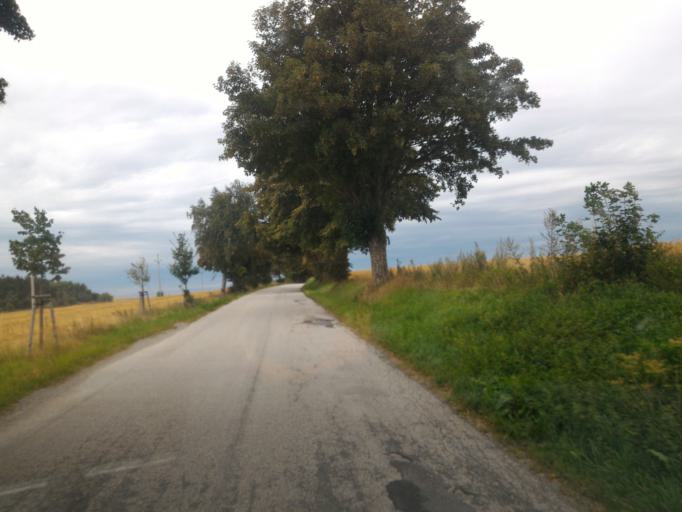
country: CZ
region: Vysocina
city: Knezice
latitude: 49.2385
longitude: 15.5927
